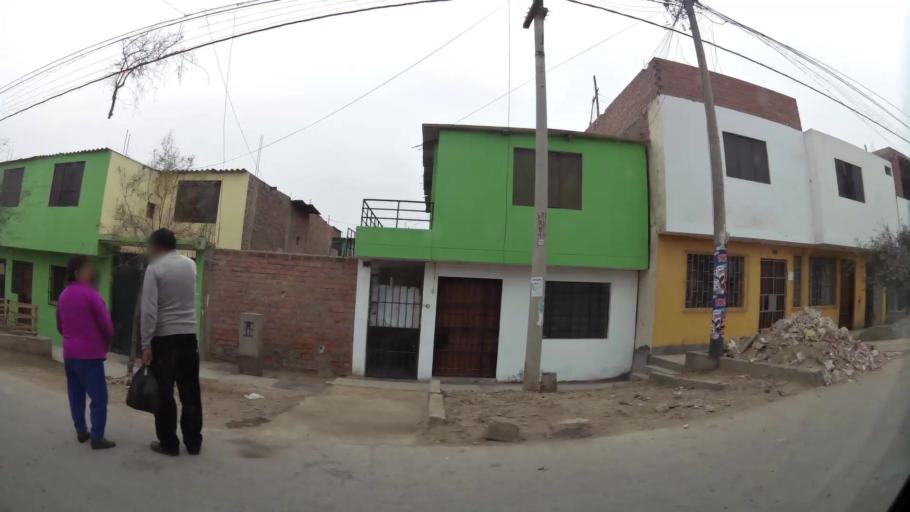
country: PE
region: Lima
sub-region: Lima
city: Surco
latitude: -12.2049
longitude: -76.9791
